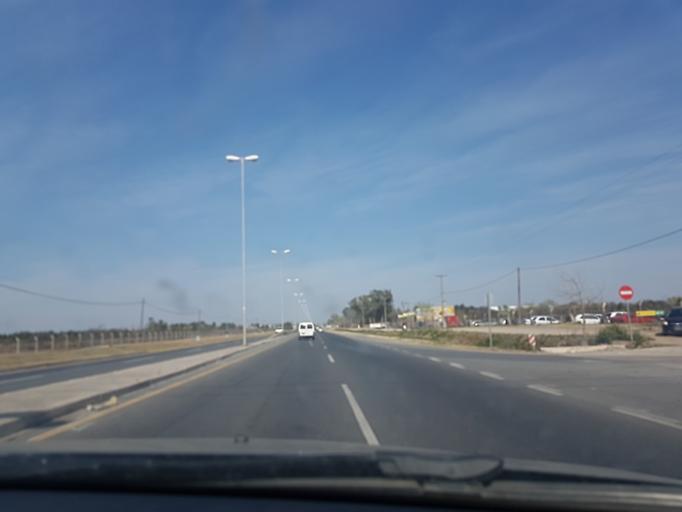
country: AR
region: Cordoba
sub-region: Departamento de Capital
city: Cordoba
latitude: -31.4883
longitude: -64.2486
